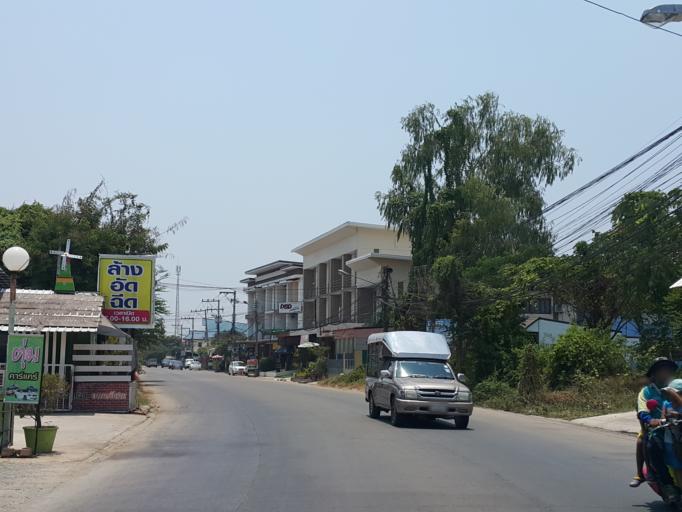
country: TH
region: Phitsanulok
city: Phitsanulok
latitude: 16.8117
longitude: 100.2456
